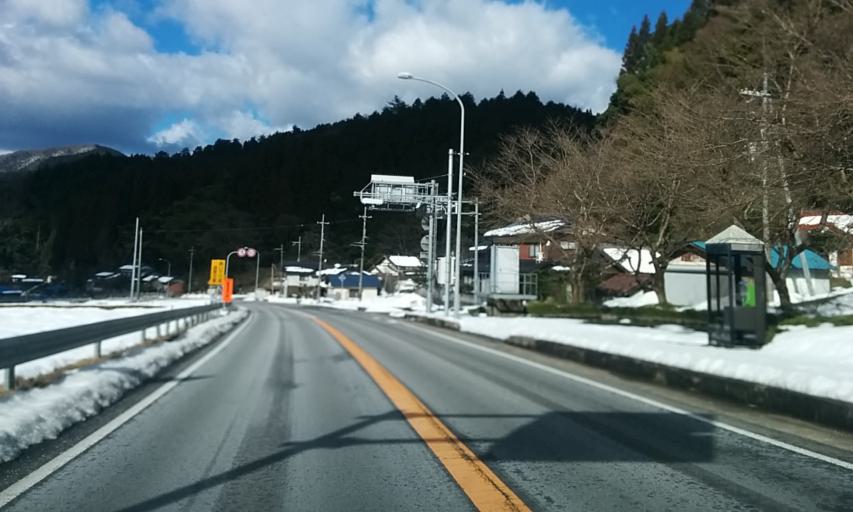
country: JP
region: Kyoto
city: Fukuchiyama
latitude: 35.4167
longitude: 135.0384
